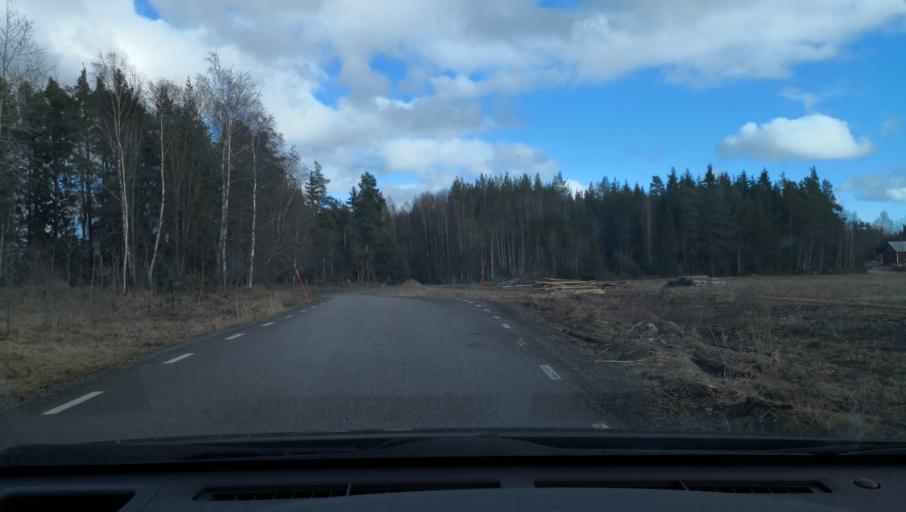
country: SE
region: Vaestmanland
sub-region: Arboga Kommun
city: Arboga
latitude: 59.3390
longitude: 15.7009
